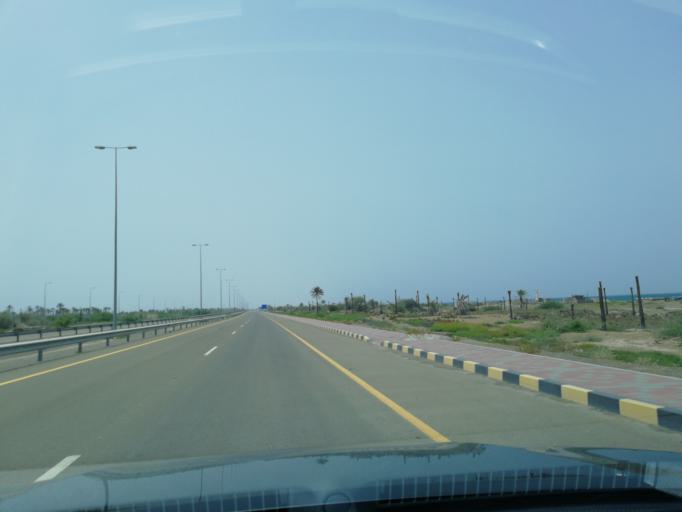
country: OM
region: Al Batinah
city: Al Liwa'
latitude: 24.6317
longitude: 56.5271
